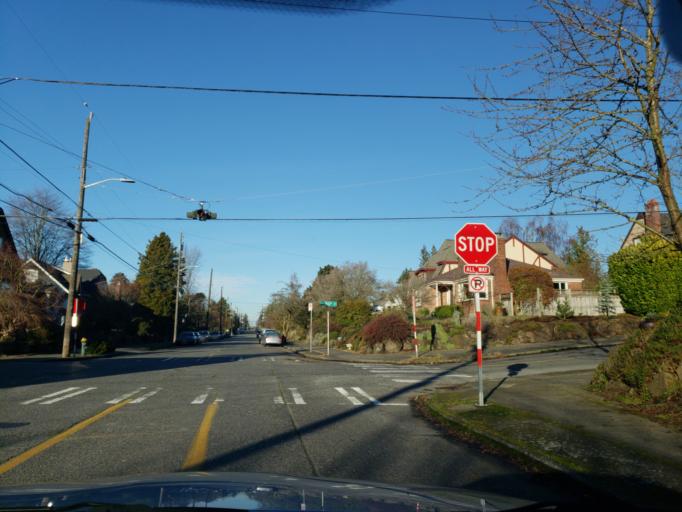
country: US
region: Washington
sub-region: King County
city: Lake Forest Park
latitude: 47.6865
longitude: -122.3068
